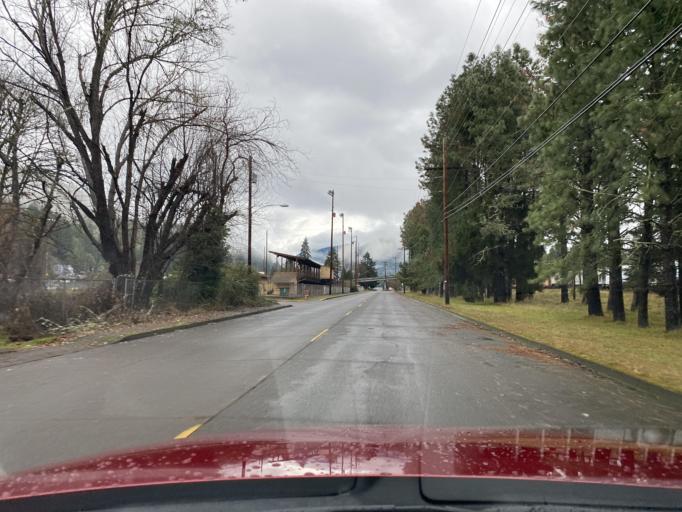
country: US
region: Oregon
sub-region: Lane County
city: Oakridge
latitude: 43.7473
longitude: -122.4709
